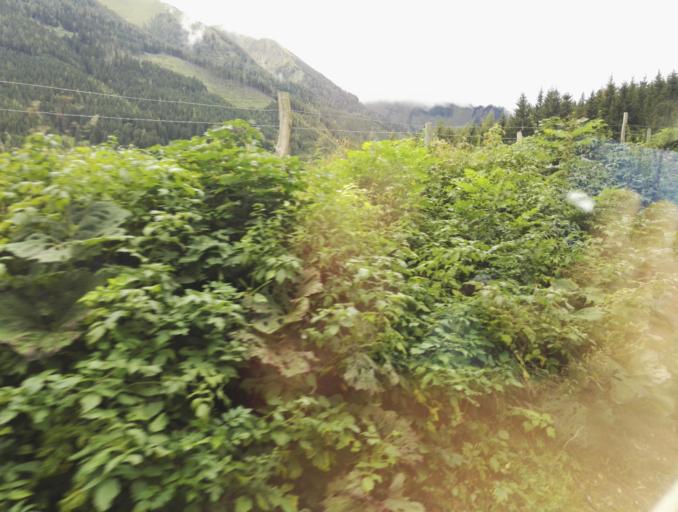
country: AT
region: Styria
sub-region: Politischer Bezirk Leoben
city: Vordernberg
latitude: 47.5094
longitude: 14.9833
